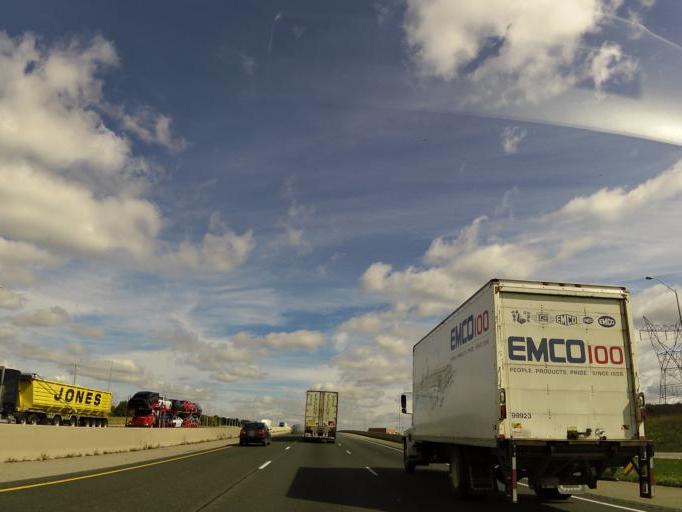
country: CA
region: Ontario
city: Dorchester
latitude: 42.9722
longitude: -80.9740
